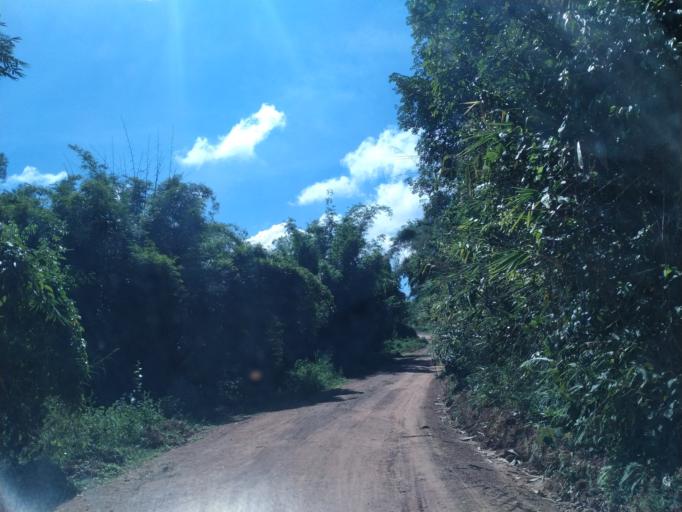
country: LA
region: Vientiane
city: Muang Phon-Hong
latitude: 18.6279
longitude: 102.8777
